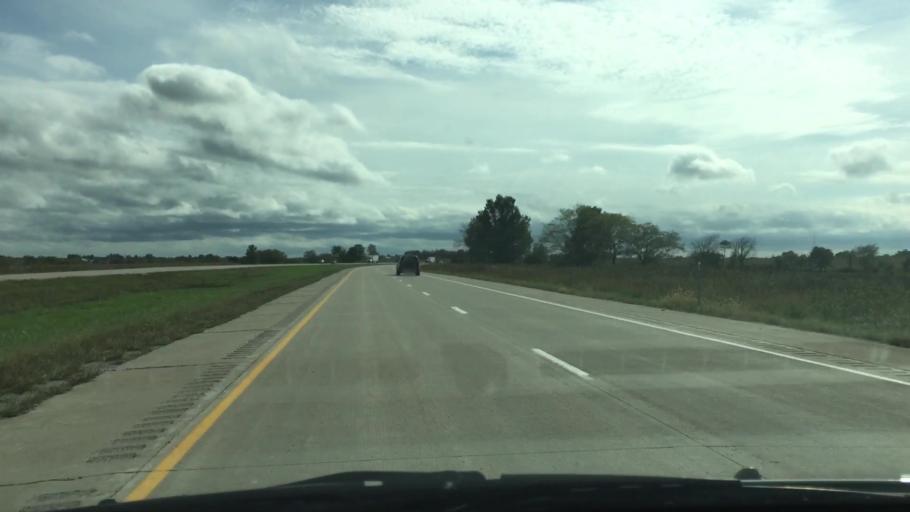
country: US
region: Iowa
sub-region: Decatur County
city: Leon
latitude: 40.8474
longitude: -93.8044
